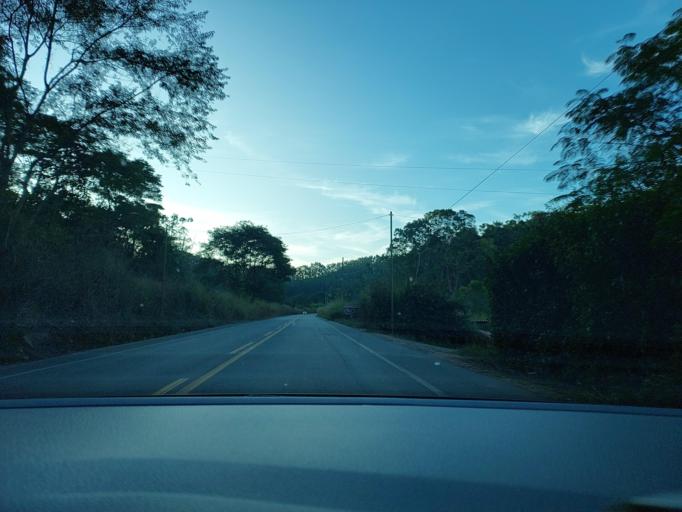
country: BR
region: Minas Gerais
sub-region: Vicosa
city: Vicosa
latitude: -20.8166
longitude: -42.8257
